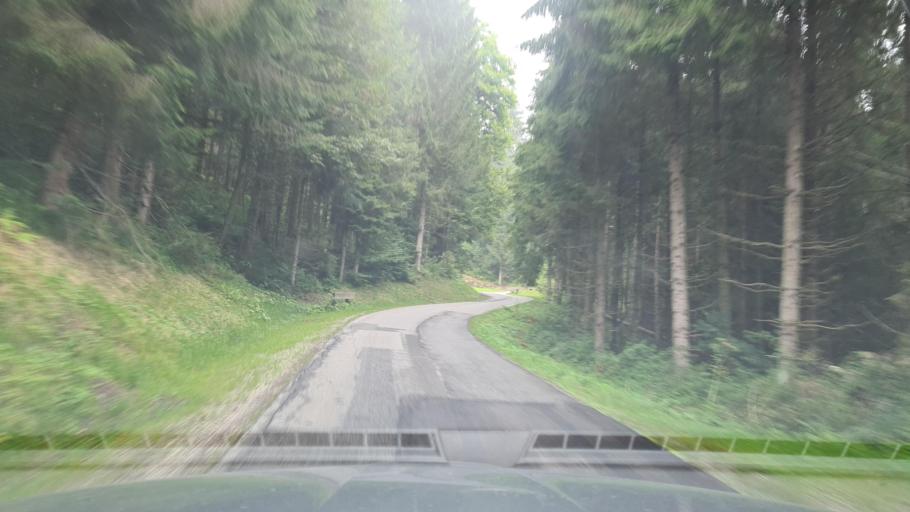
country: AT
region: Salzburg
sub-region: Politischer Bezirk Sankt Johann im Pongau
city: Sankt Johann im Pongau
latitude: 47.3587
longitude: 13.1830
